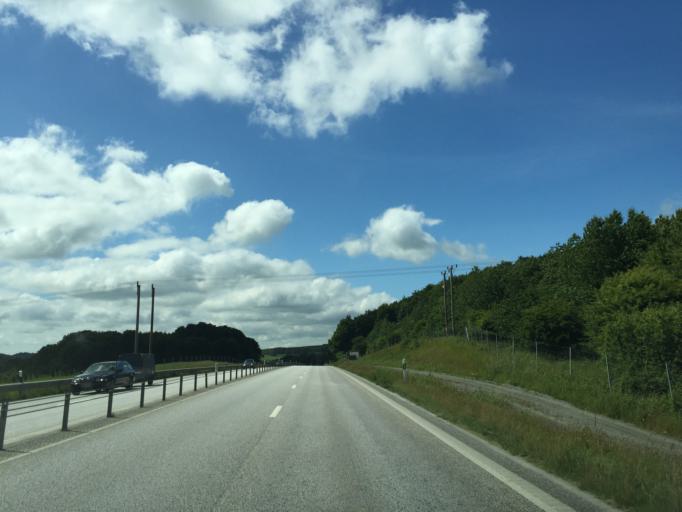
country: SE
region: Skane
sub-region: Skurups Kommun
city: Skurup
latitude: 55.4943
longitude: 13.4506
